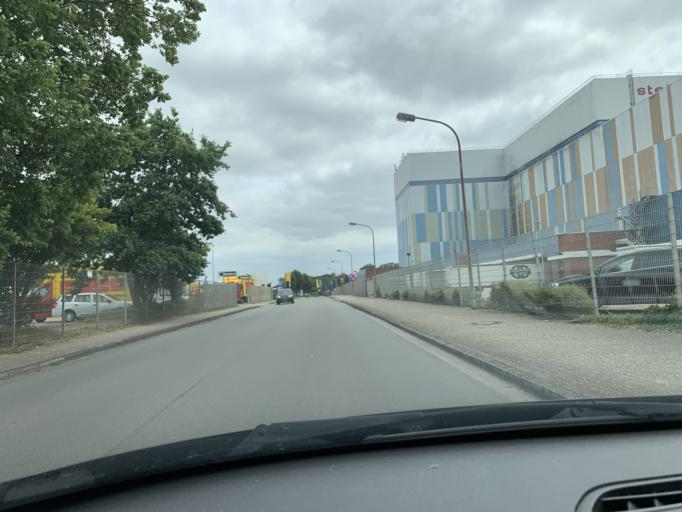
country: DE
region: Lower Saxony
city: Westerstede
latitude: 53.2651
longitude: 7.9382
